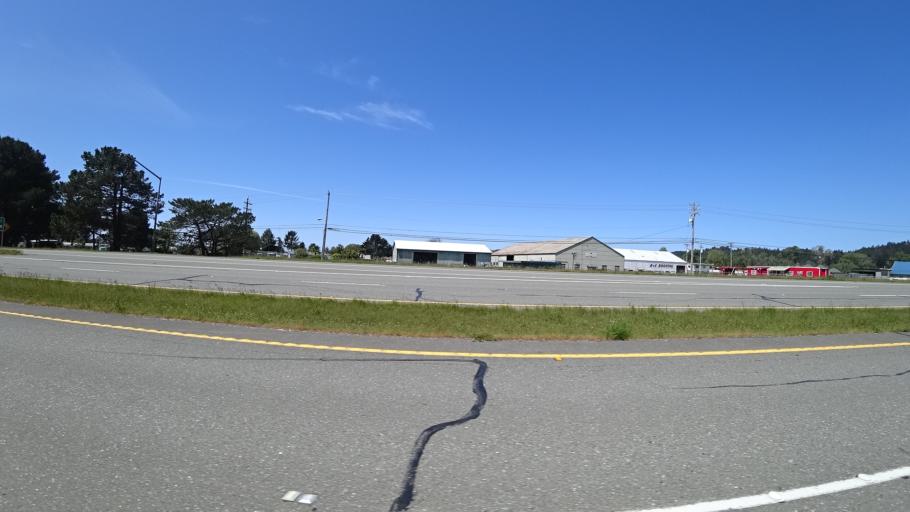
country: US
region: California
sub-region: Humboldt County
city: Arcata
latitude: 40.9066
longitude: -124.0729
